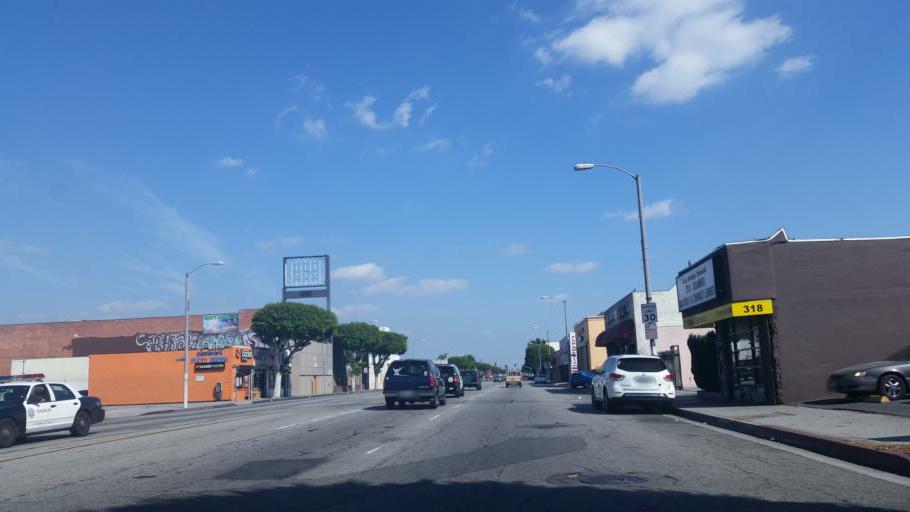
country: US
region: California
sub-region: Los Angeles County
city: Compton
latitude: 33.8959
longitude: -118.2195
